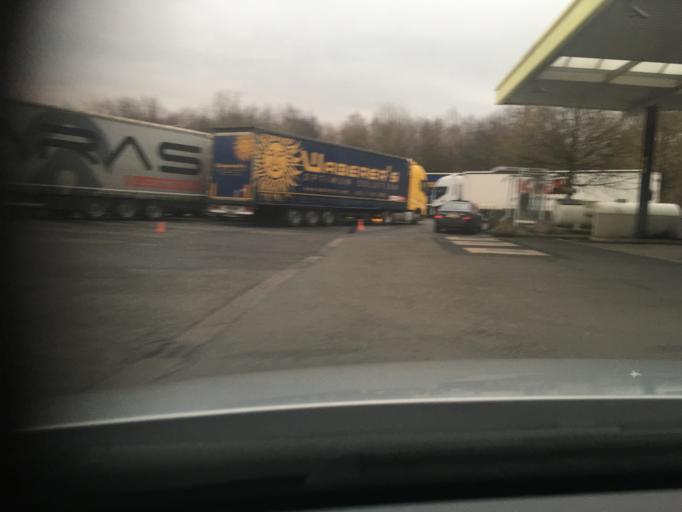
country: DE
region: North Rhine-Westphalia
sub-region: Regierungsbezirk Koln
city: Neustadt/Sued
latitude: 50.8878
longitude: 6.9248
